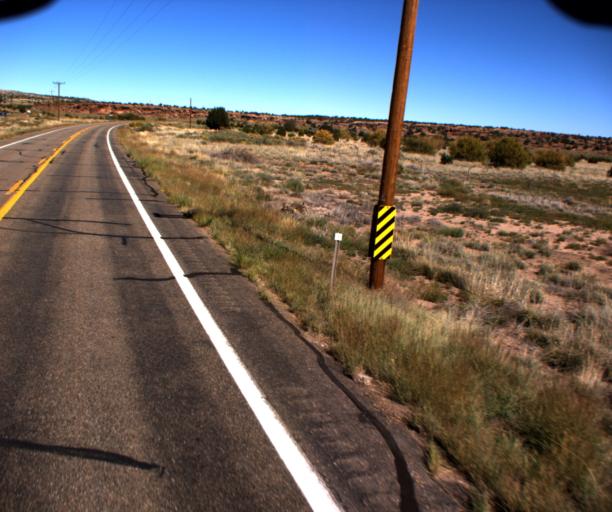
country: US
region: Arizona
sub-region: Apache County
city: Saint Johns
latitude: 34.4449
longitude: -109.4106
